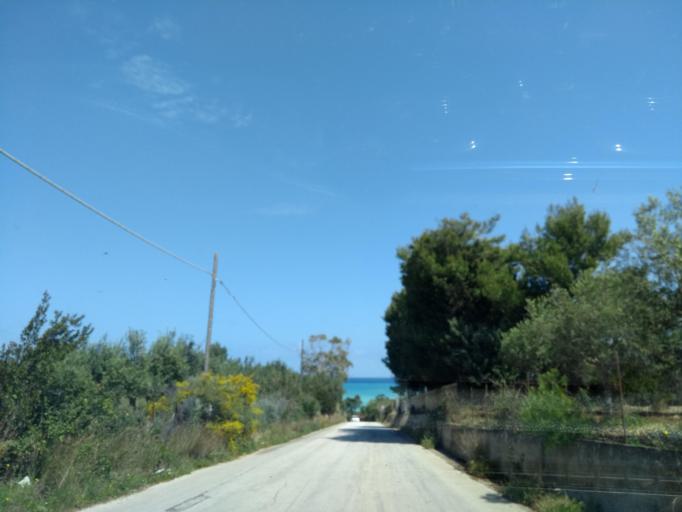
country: IT
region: Sicily
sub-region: Trapani
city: Castellammare del Golfo
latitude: 38.0539
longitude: 12.8412
